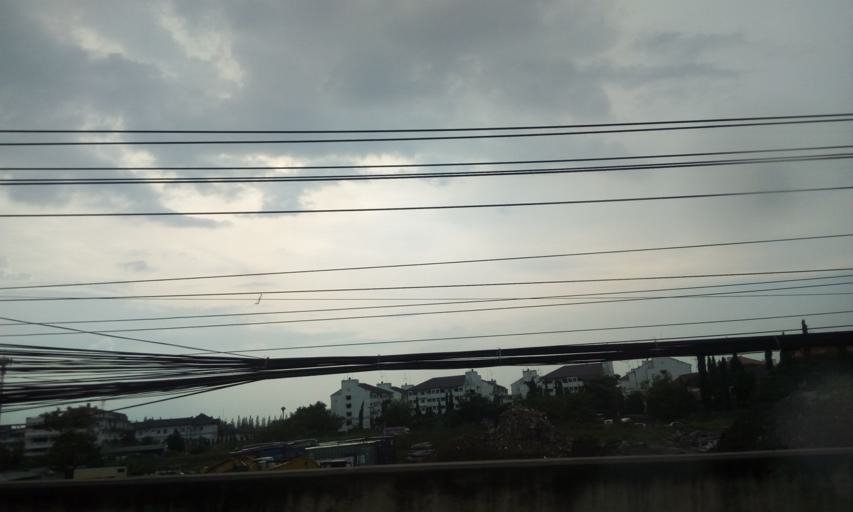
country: TH
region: Phra Nakhon Si Ayutthaya
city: Ban Bang Kadi Pathum Thani
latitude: 13.9697
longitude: 100.5503
